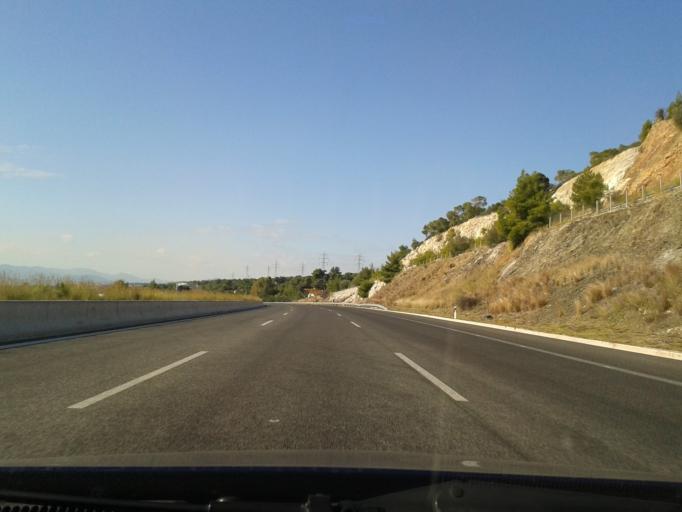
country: GR
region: Peloponnese
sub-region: Nomos Korinthias
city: Agioi Theodoroi
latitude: 37.9501
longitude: 23.1662
